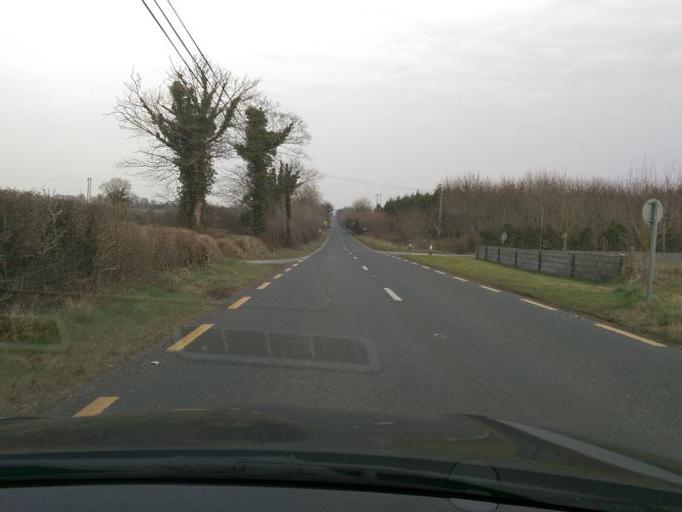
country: IE
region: Connaught
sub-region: Roscommon
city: Roscommon
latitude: 53.5168
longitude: -8.3443
